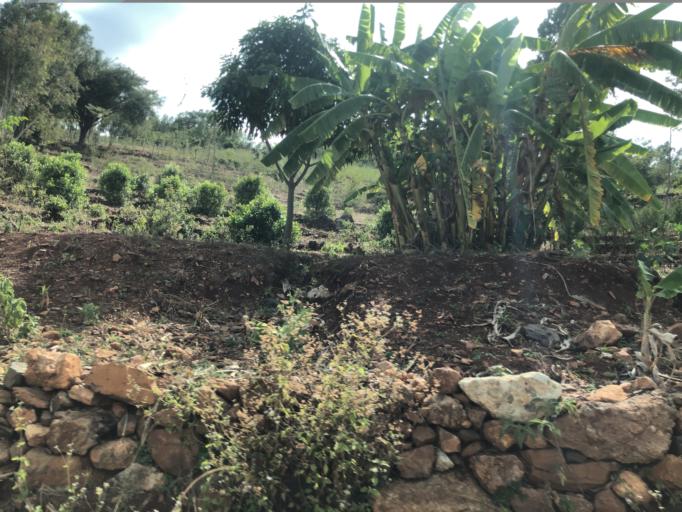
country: ET
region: Southern Nations, Nationalities, and People's Region
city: Konso
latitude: 5.3324
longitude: 37.4304
